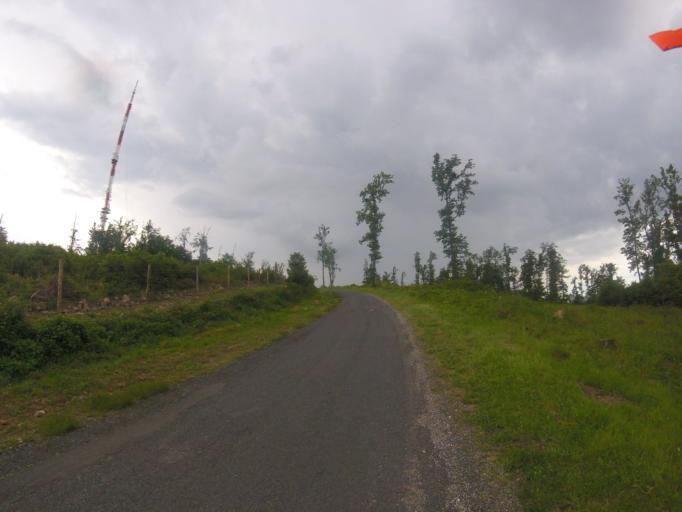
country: HU
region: Veszprem
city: Urkut
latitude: 47.0500
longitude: 17.6496
